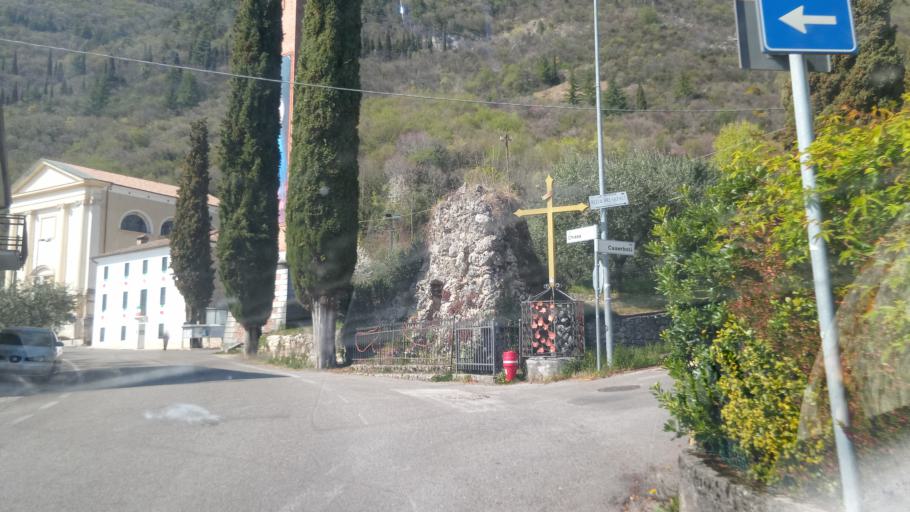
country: IT
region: Veneto
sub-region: Provincia di Treviso
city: Borso del Grappa
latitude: 45.8128
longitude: 11.7722
